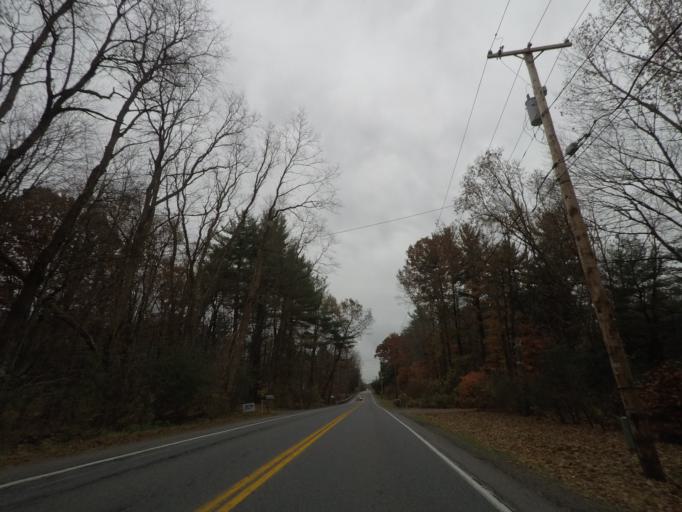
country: US
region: New York
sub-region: Saratoga County
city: Country Knolls
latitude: 42.8553
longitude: -73.8202
